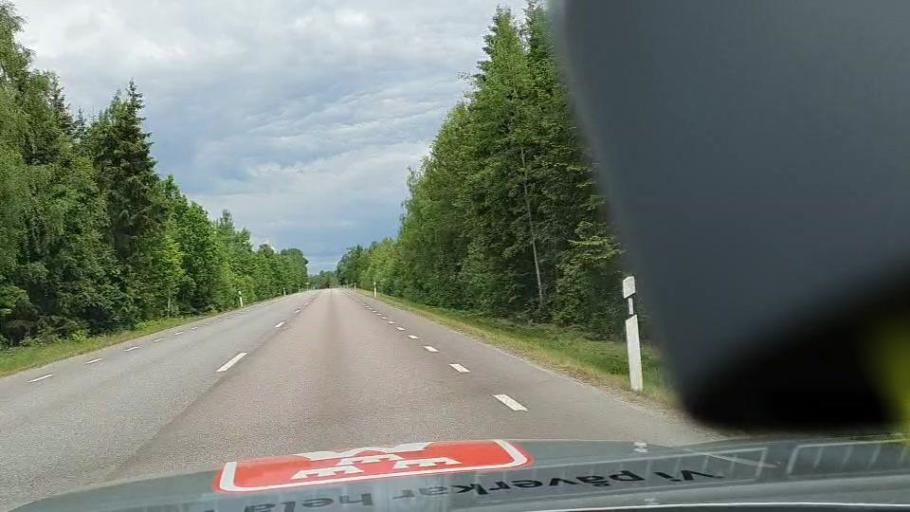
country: SE
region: Blekinge
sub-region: Karlskrona Kommun
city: Rodeby
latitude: 56.4363
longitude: 15.5446
